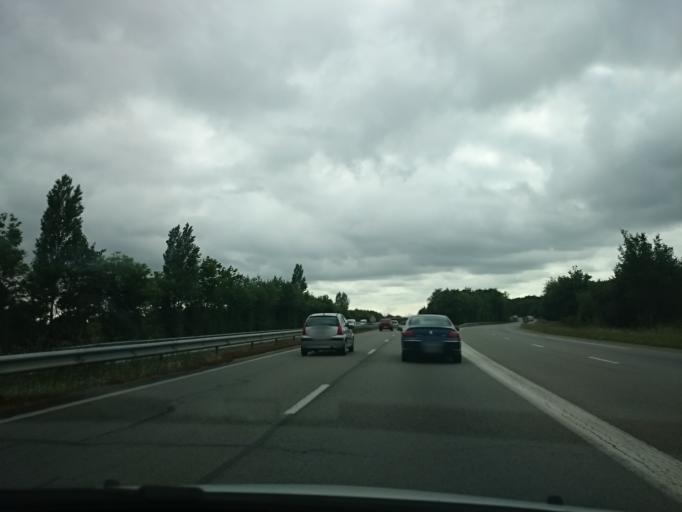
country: FR
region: Pays de la Loire
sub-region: Departement de la Loire-Atlantique
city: La Montagne
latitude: 47.1724
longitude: -1.6677
